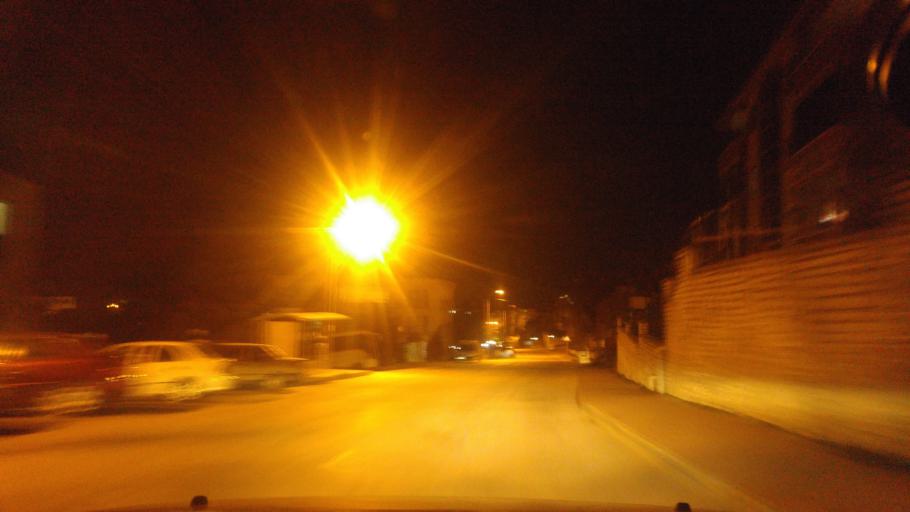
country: TR
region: Karabuk
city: Safranbolu
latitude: 41.2620
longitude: 32.6811
